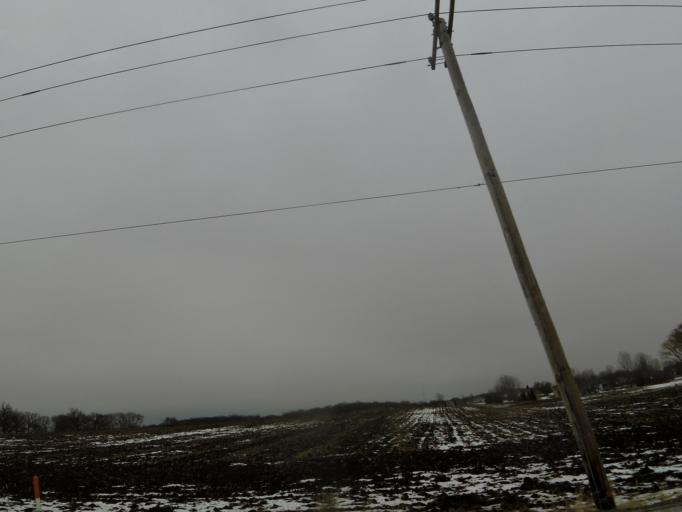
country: US
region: Minnesota
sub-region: Carver County
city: Cologne
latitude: 44.7805
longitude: -93.7881
